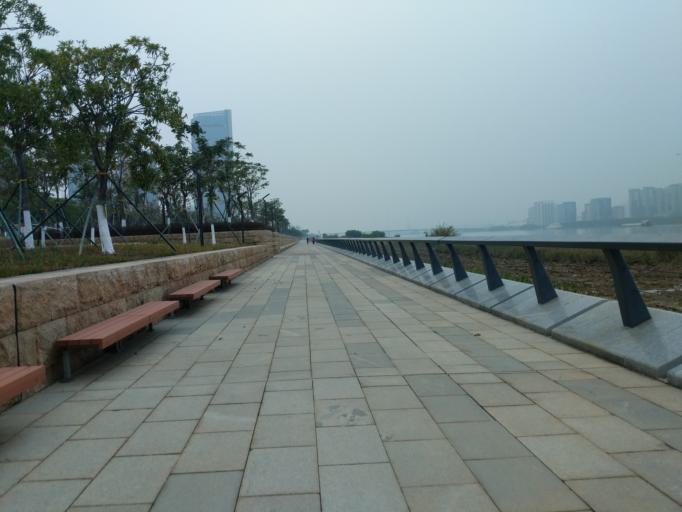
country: CN
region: Guangdong
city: Hengli
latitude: 22.7683
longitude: 113.5235
